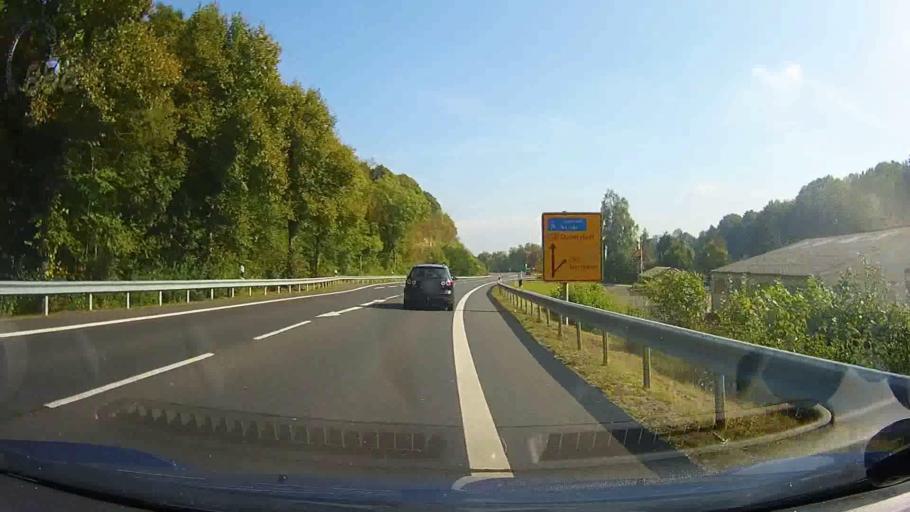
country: DE
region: Lower Saxony
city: Hardegsen
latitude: 51.6476
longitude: 9.8417
